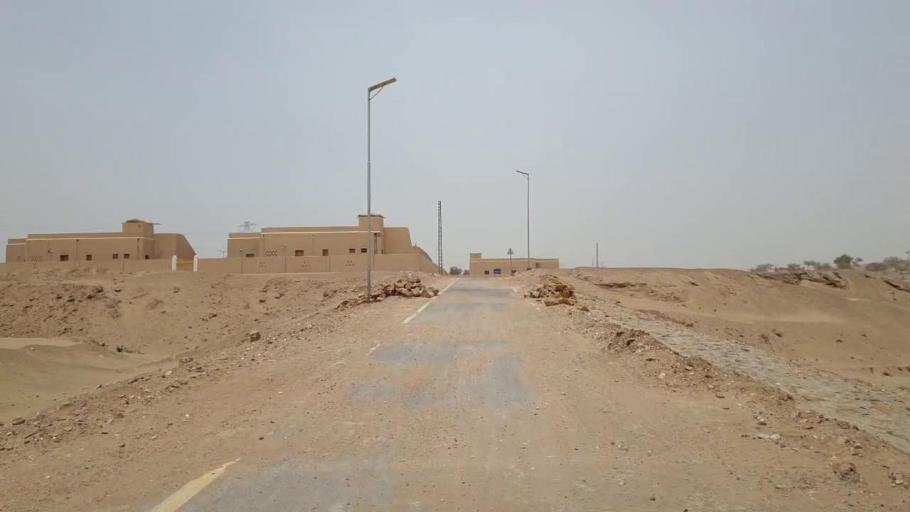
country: PK
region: Sindh
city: Islamkot
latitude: 24.7223
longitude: 70.3319
